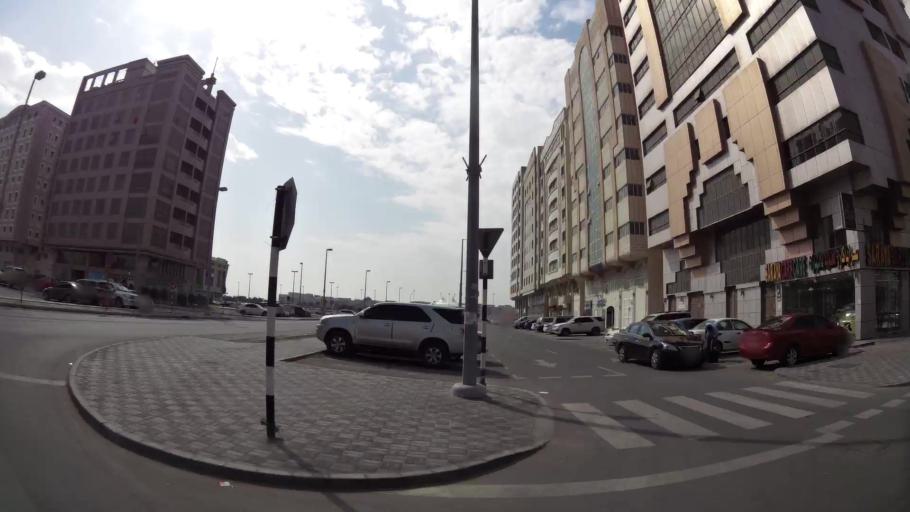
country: AE
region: Abu Dhabi
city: Abu Dhabi
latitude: 24.3336
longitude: 54.5323
